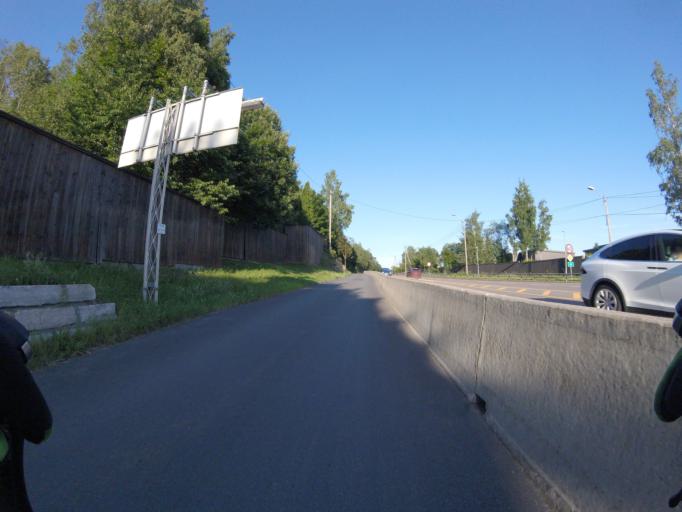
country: NO
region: Akershus
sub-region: Lorenskog
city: Kjenn
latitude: 59.9600
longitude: 10.8881
